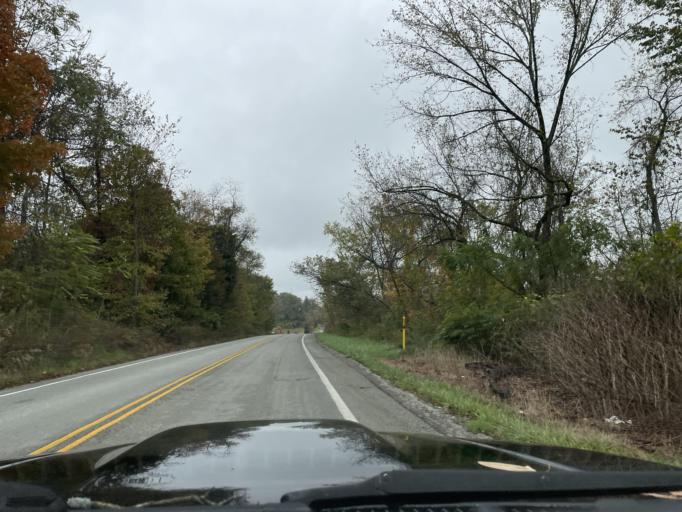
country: US
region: Pennsylvania
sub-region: Allegheny County
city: Springdale
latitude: 40.5300
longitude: -79.7861
